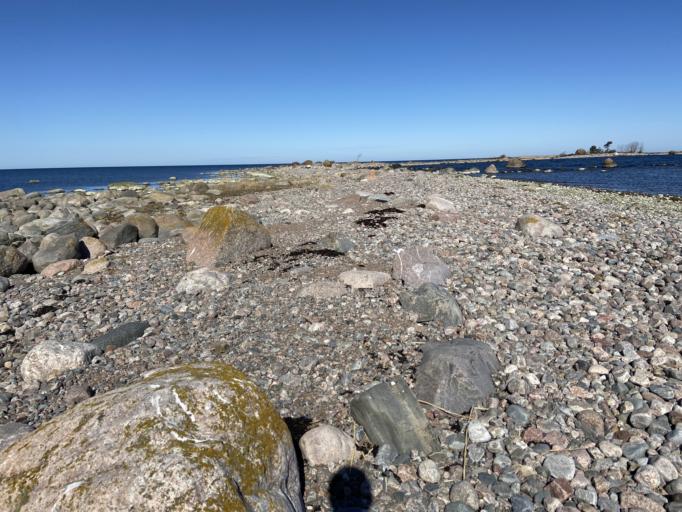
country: EE
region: Harju
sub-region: Loksa linn
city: Loksa
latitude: 59.6689
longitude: 25.6965
